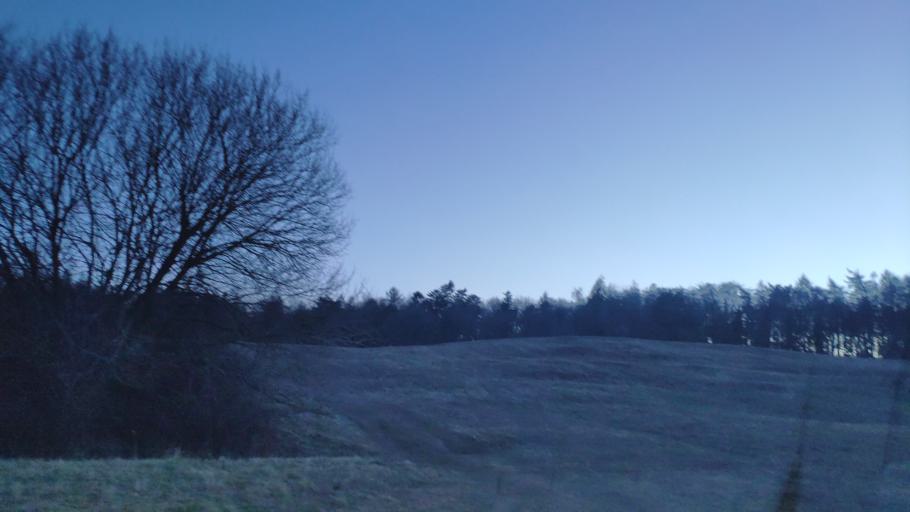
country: SK
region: Kosicky
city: Kosice
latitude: 48.8337
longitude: 21.2571
